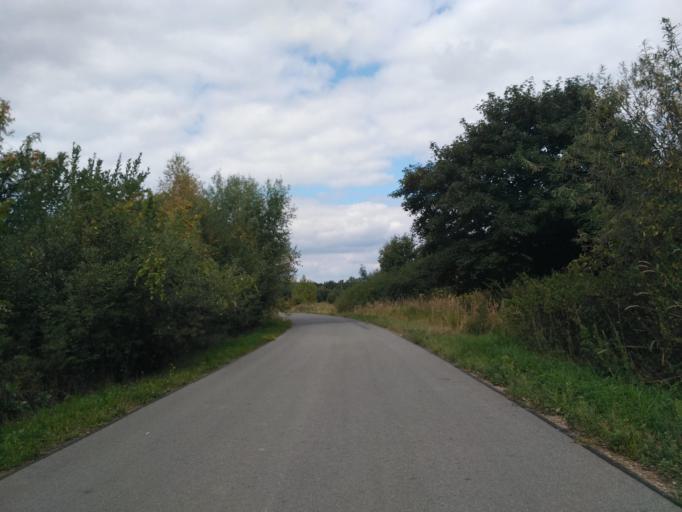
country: PL
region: Subcarpathian Voivodeship
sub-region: Powiat rzeszowski
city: Dynow
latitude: 49.7714
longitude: 22.2831
